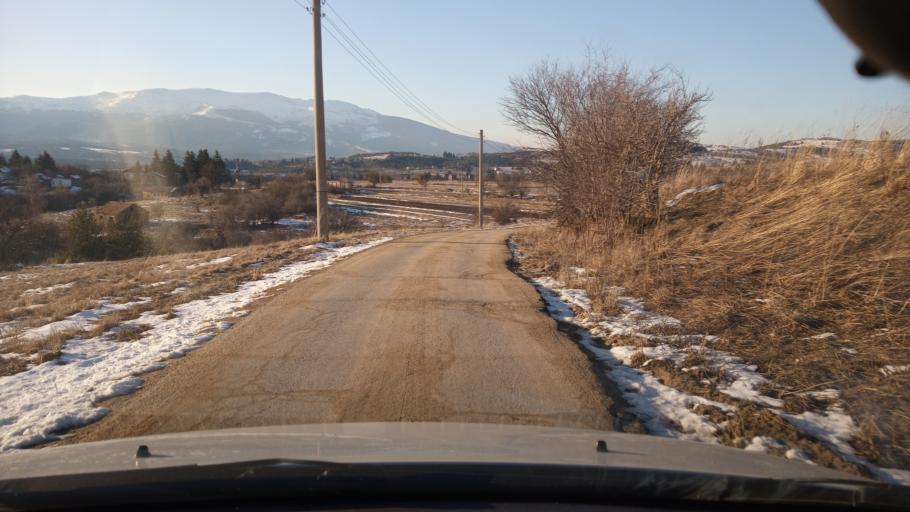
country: BG
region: Sofiya
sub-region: Obshtina Samokov
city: Samokov
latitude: 42.4792
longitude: 23.4183
